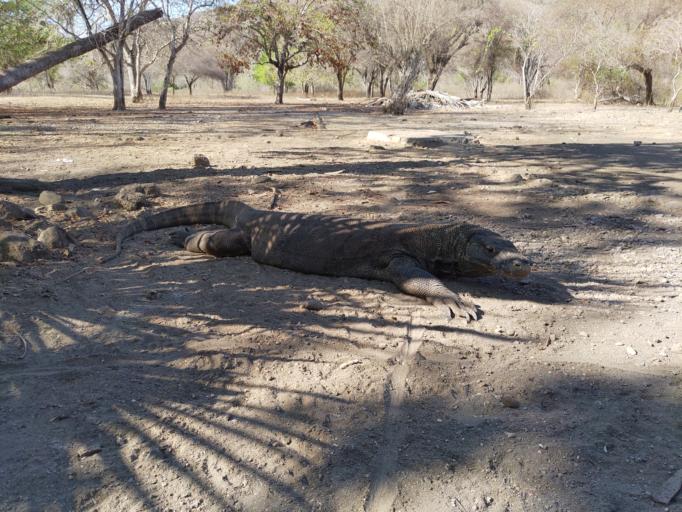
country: ID
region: East Nusa Tenggara
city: Komodo
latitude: -8.5714
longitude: 119.4975
